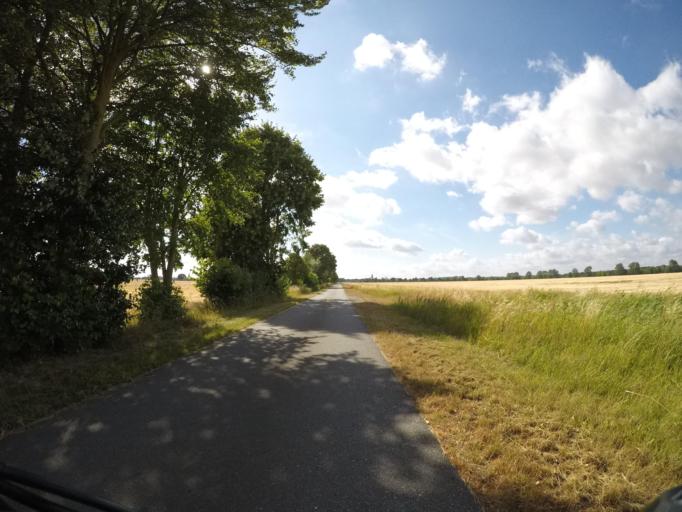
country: DE
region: Lower Saxony
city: Damnatz
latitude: 53.1817
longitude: 11.1666
